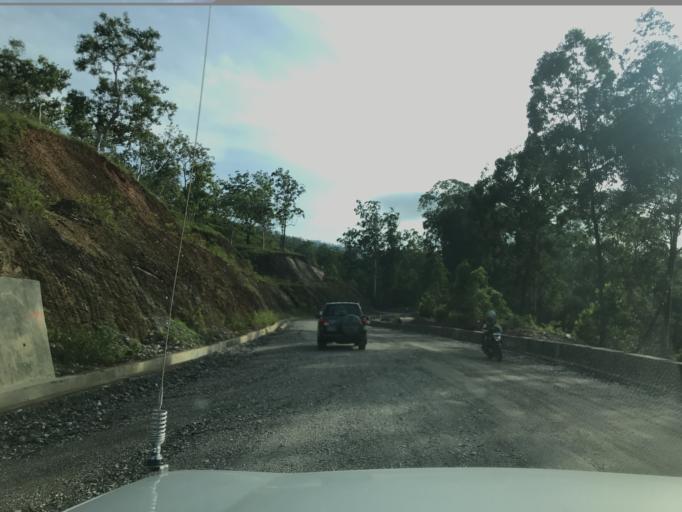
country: TL
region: Aileu
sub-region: Aileu Villa
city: Aileu
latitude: -8.6646
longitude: 125.5394
